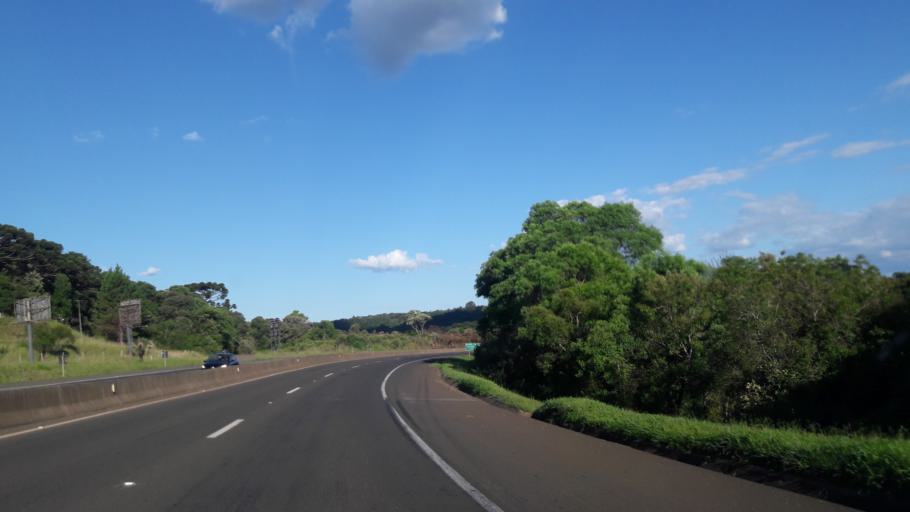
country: BR
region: Parana
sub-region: Guarapuava
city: Guarapuava
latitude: -25.3396
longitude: -51.4172
